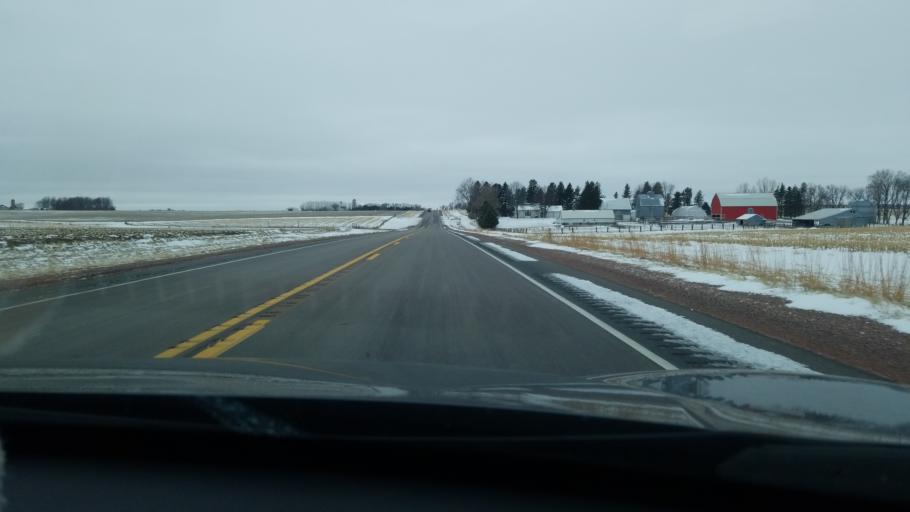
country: US
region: Iowa
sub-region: Lyon County
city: Rock Rapids
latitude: 43.4331
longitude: -96.3749
